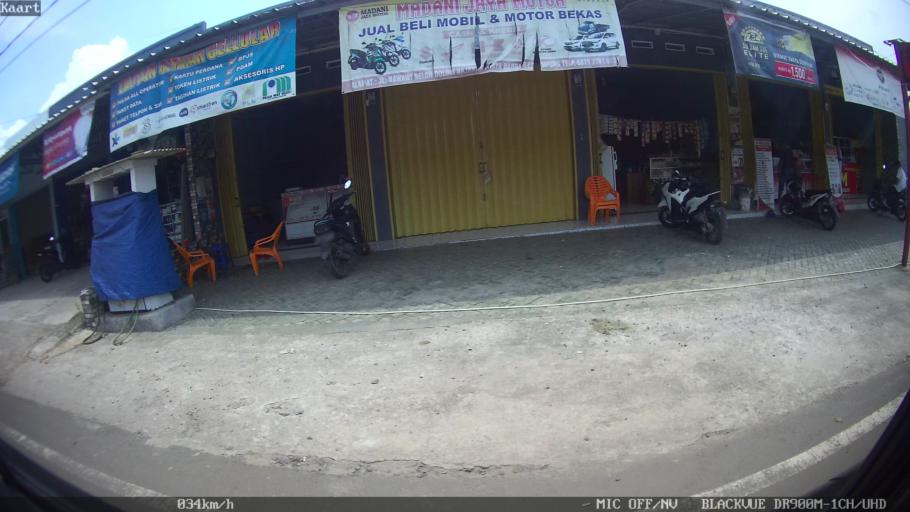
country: ID
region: Lampung
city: Kedaton
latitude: -5.3434
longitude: 105.2437
